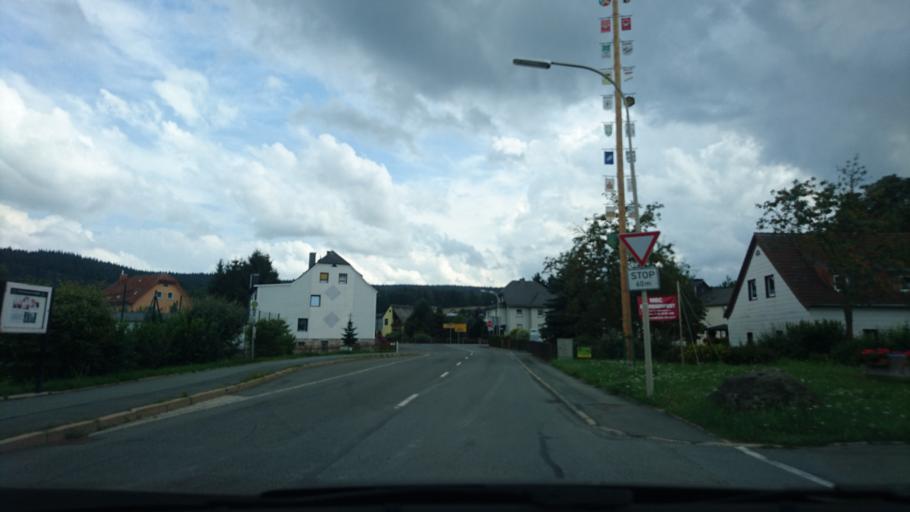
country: DE
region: Bavaria
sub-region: Upper Franconia
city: Lichtenberg
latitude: 50.3576
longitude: 11.6839
